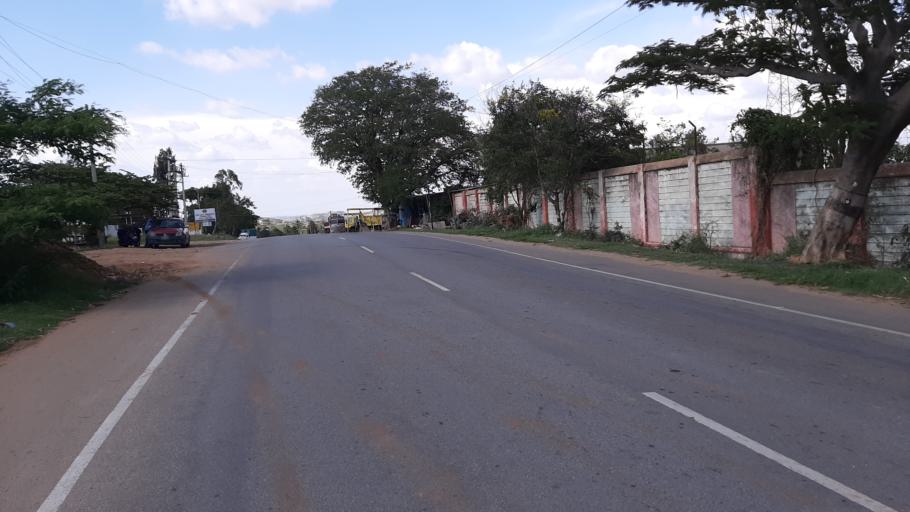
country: IN
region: Tamil Nadu
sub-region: Krishnagiri
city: Denkanikota
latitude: 12.5382
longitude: 77.7888
